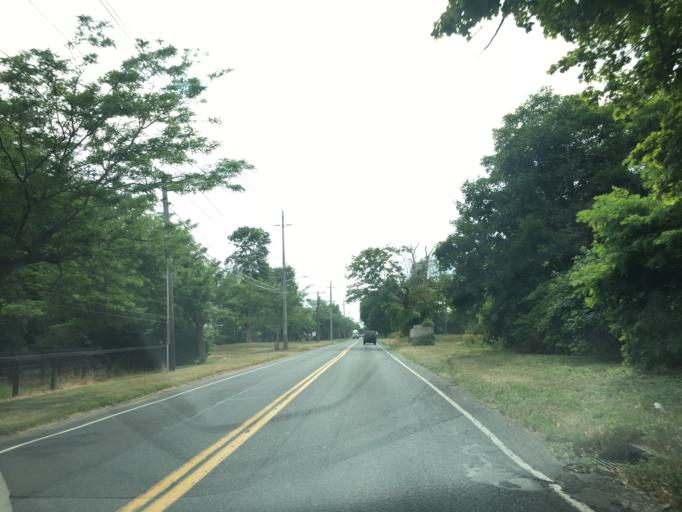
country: US
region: New York
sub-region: Suffolk County
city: Laurel
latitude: 40.9847
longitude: -72.5831
